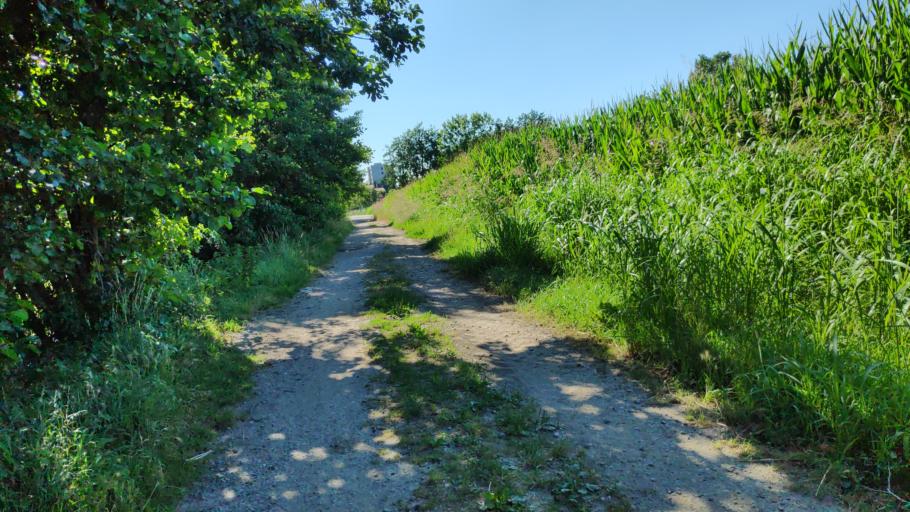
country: IT
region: Lombardy
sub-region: Citta metropolitana di Milano
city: Melzo
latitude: 45.5008
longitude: 9.4388
